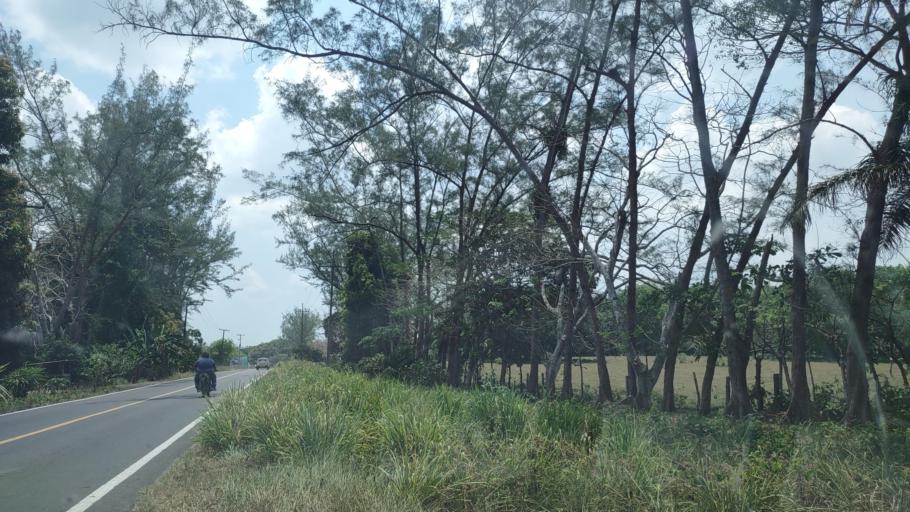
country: MX
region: Veracruz
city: Las Choapas
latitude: 17.9268
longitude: -94.1408
